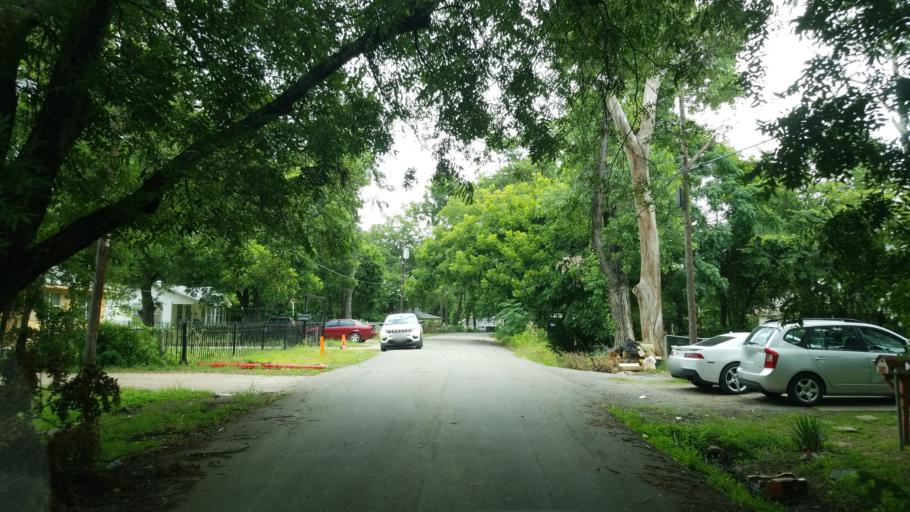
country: US
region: Texas
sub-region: Dallas County
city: Cockrell Hill
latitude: 32.7921
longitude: -96.8935
